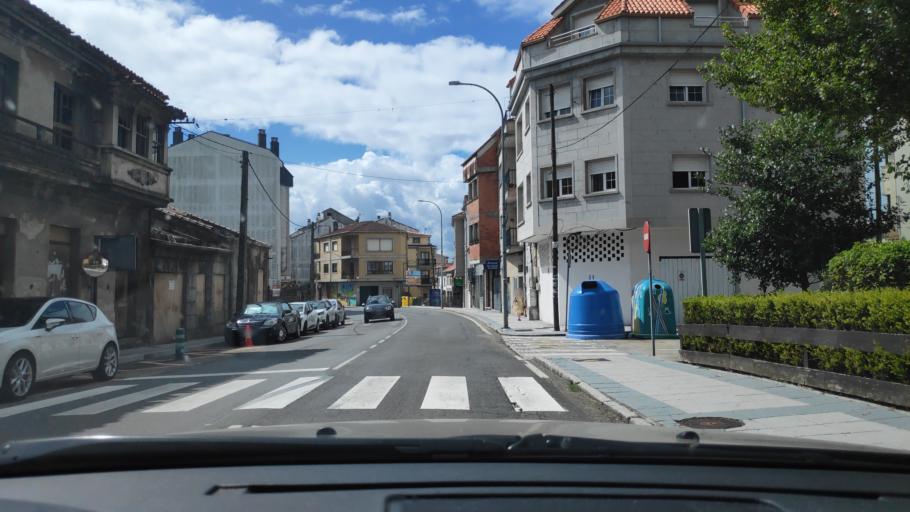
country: ES
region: Galicia
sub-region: Provincia de Pontevedra
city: Caldas de Reis
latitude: 42.6084
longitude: -8.6452
